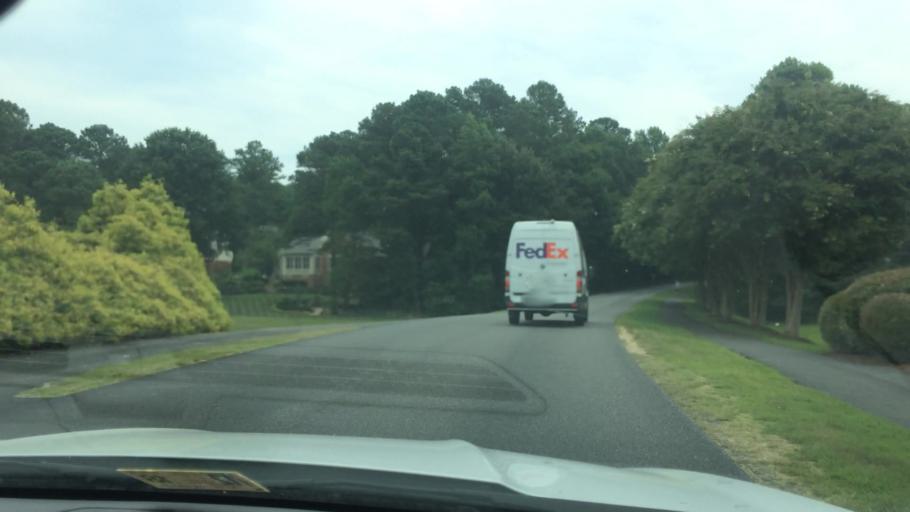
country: US
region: Virginia
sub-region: James City County
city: Williamsburg
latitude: 37.2942
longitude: -76.7887
